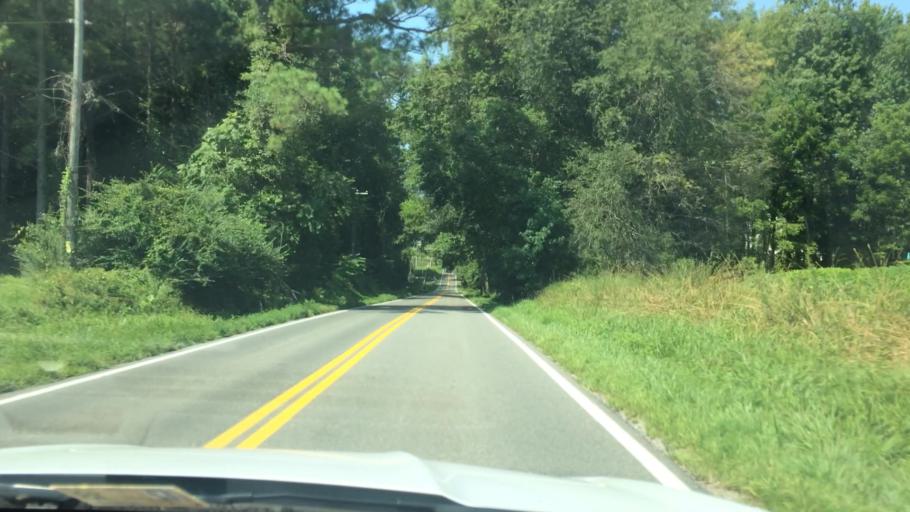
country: US
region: Virginia
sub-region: New Kent County
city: New Kent
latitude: 37.5246
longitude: -77.0482
